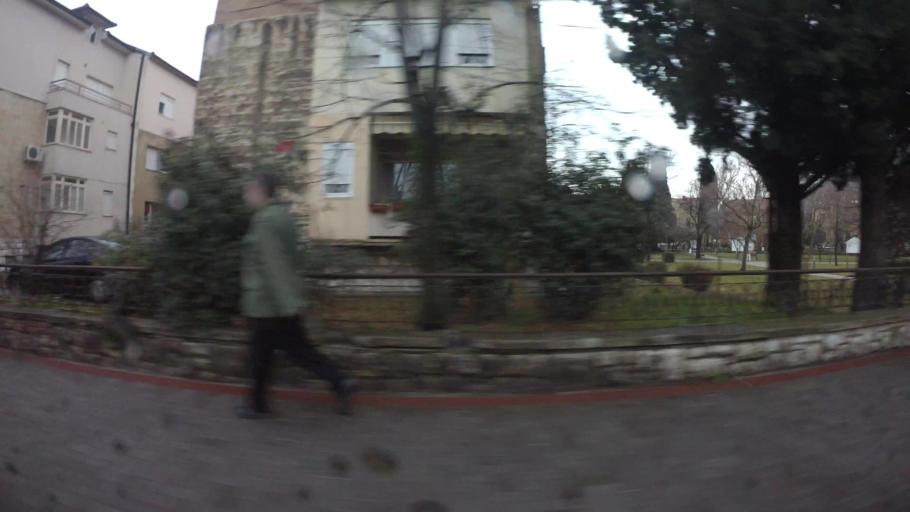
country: BA
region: Federation of Bosnia and Herzegovina
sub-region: Hercegovacko-Bosanski Kanton
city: Mostar
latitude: 43.3427
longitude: 17.8034
